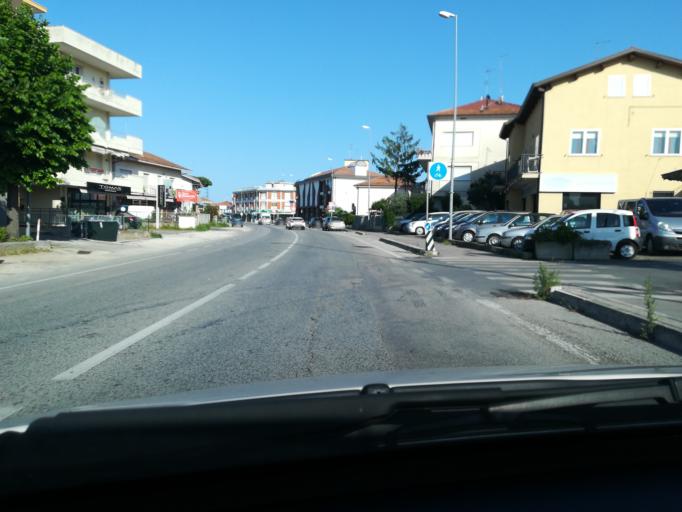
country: IT
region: Emilia-Romagna
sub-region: Provincia di Rimini
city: Riccione
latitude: 43.9922
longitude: 12.6534
